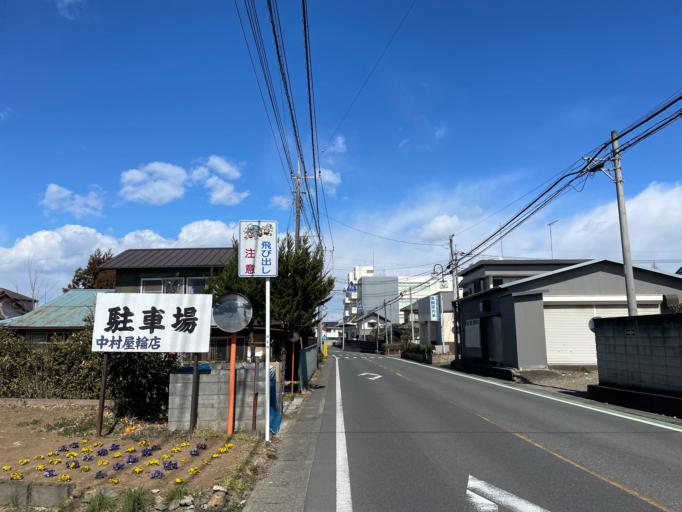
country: JP
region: Saitama
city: Sakado
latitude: 35.9757
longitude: 139.4171
